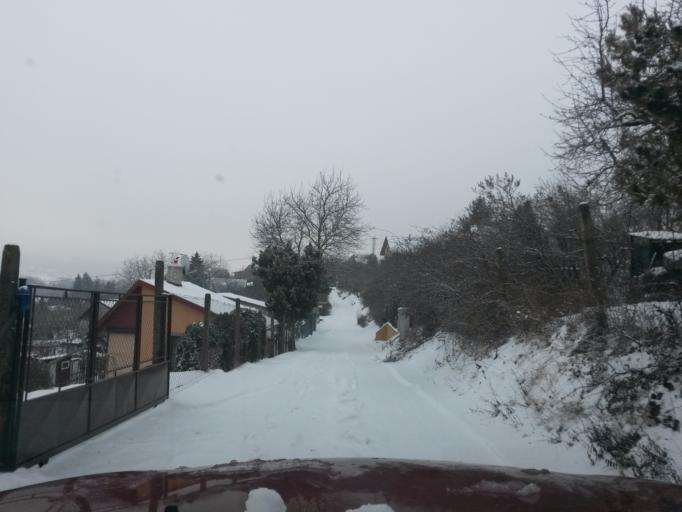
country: SK
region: Kosicky
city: Kosice
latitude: 48.7231
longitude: 21.3271
